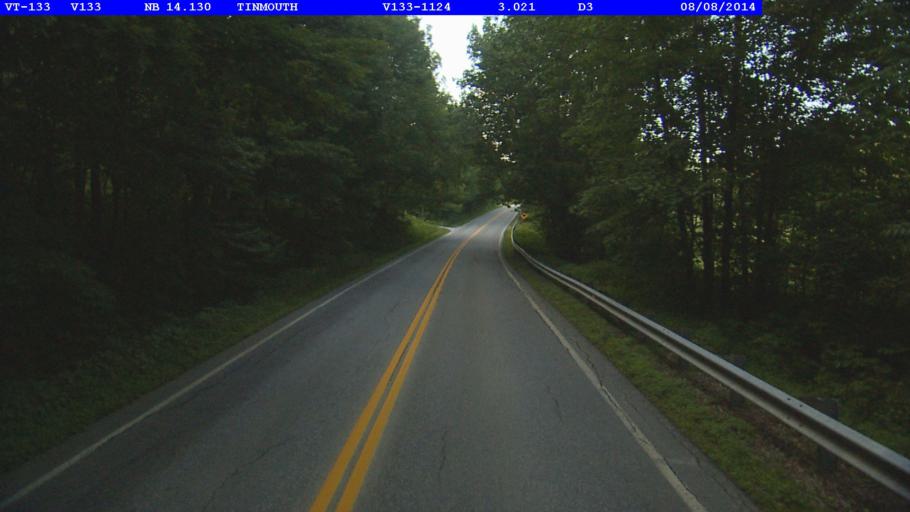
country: US
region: Vermont
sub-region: Rutland County
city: West Rutland
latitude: 43.4897
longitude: -73.0760
